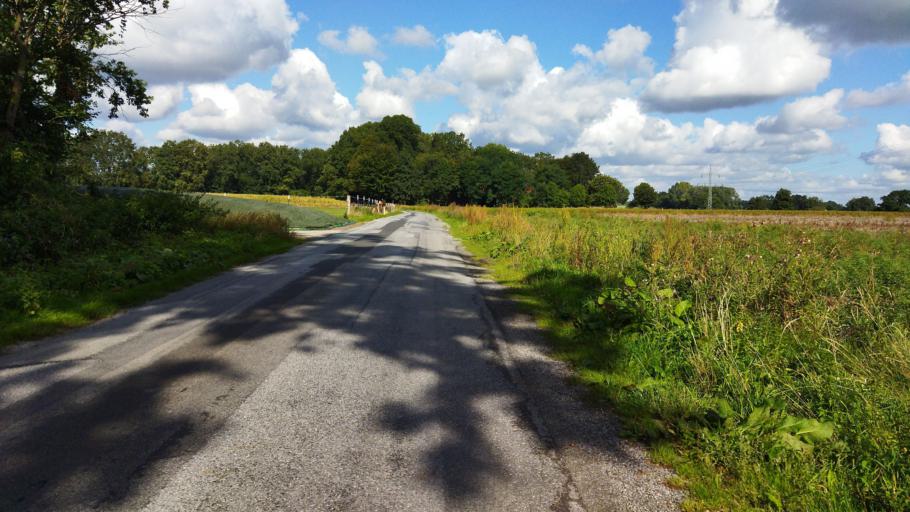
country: DE
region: Lower Saxony
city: Emsburen
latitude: 52.3943
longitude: 7.3242
